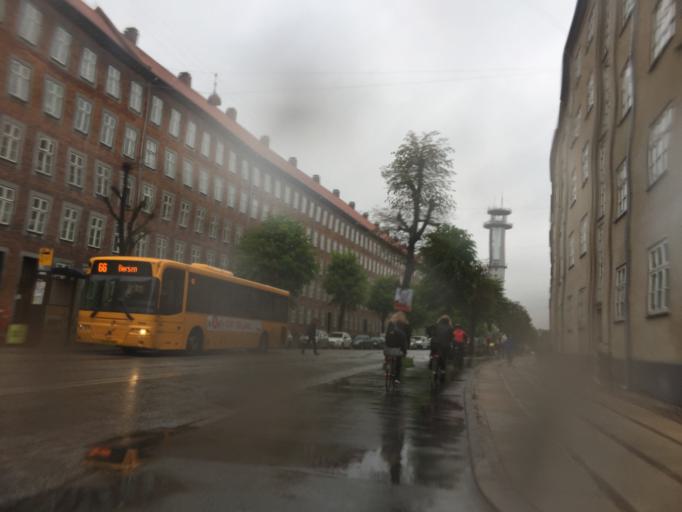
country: DK
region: Capital Region
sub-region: Frederiksberg Kommune
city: Frederiksberg
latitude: 55.6893
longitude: 12.5419
